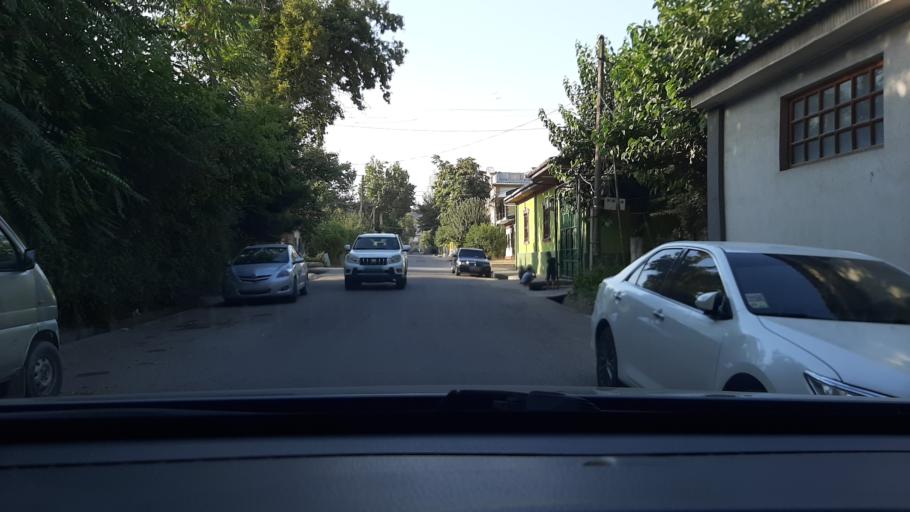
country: TJ
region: Dushanbe
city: Dushanbe
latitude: 38.5638
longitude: 68.8118
